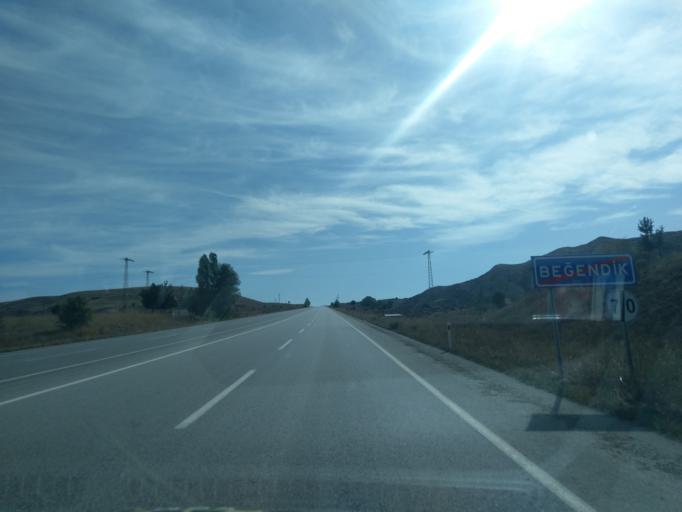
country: TR
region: Sivas
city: Imranli
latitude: 39.8846
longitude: 38.0357
